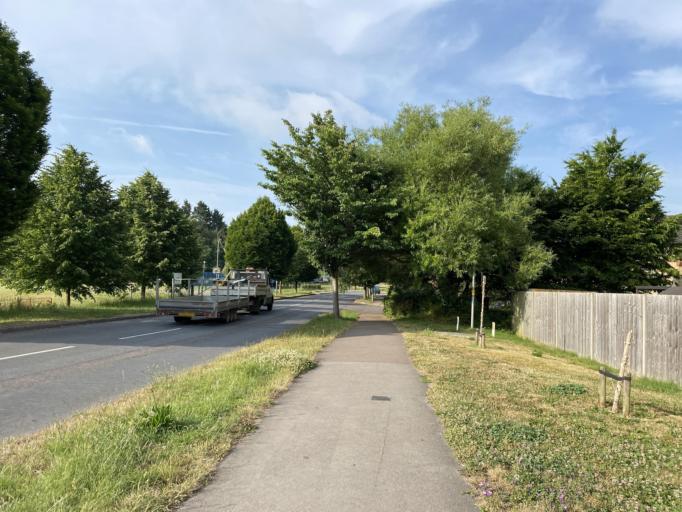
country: GB
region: England
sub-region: Suffolk
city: Haverhill
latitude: 52.0757
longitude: 0.4539
